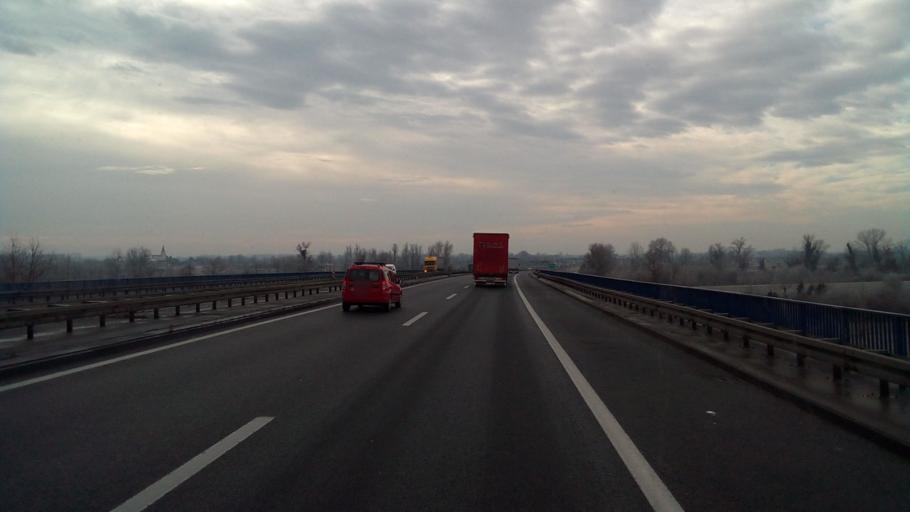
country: HR
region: Grad Zagreb
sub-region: Sesvete
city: Sesvete
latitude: 45.7844
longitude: 16.1206
